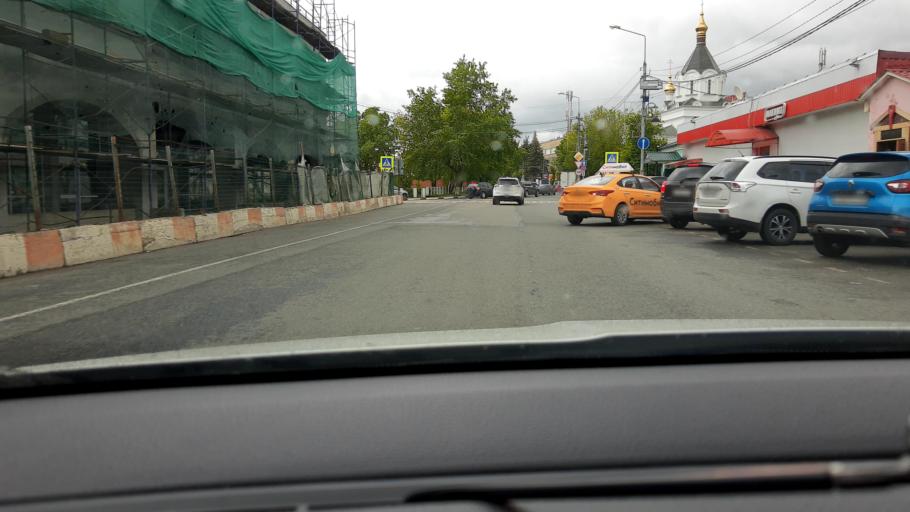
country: RU
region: Moskovskaya
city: Zvenigorod
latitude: 55.7289
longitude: 36.8617
